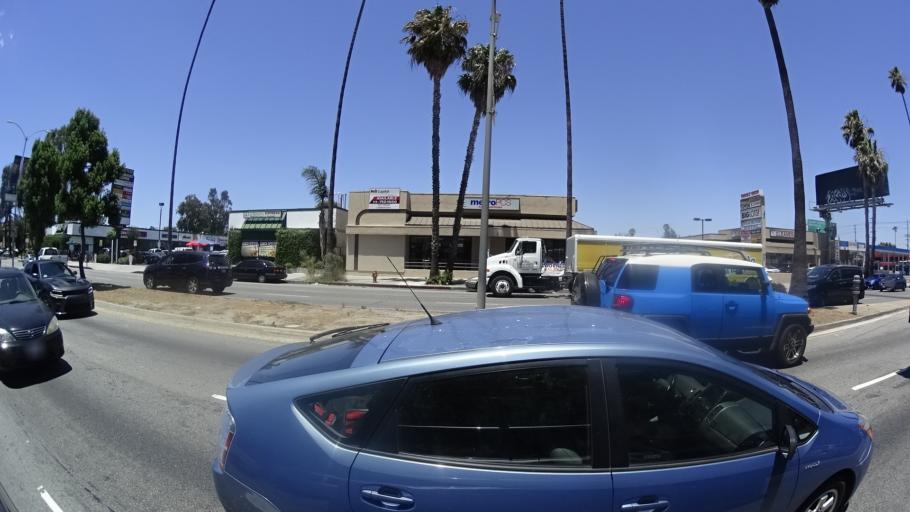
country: US
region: California
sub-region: Los Angeles County
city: Van Nuys
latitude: 34.2011
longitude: -118.4676
